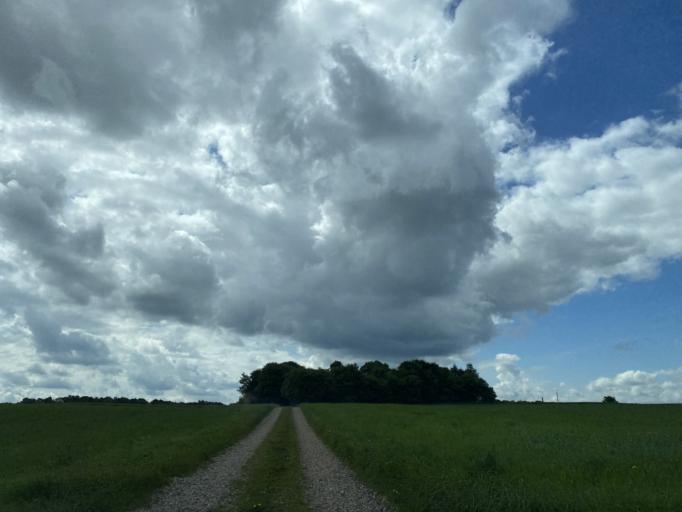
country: DK
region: Central Jutland
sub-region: Silkeborg Kommune
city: Silkeborg
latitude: 56.2125
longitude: 9.5751
